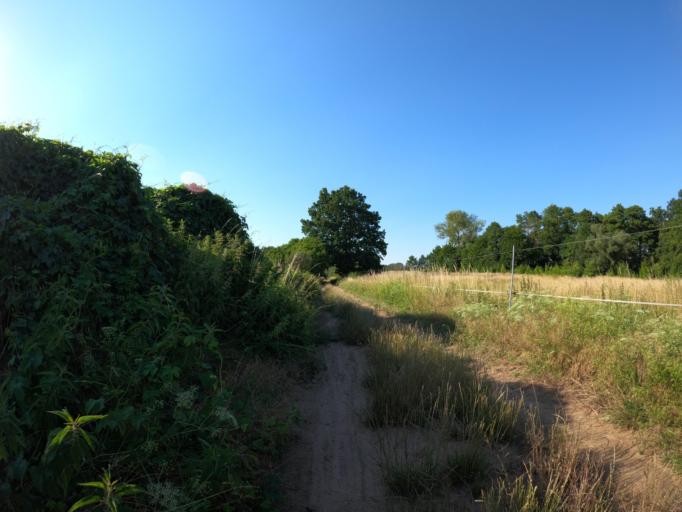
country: DE
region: Brandenburg
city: Gartz
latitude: 53.2300
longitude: 14.3681
